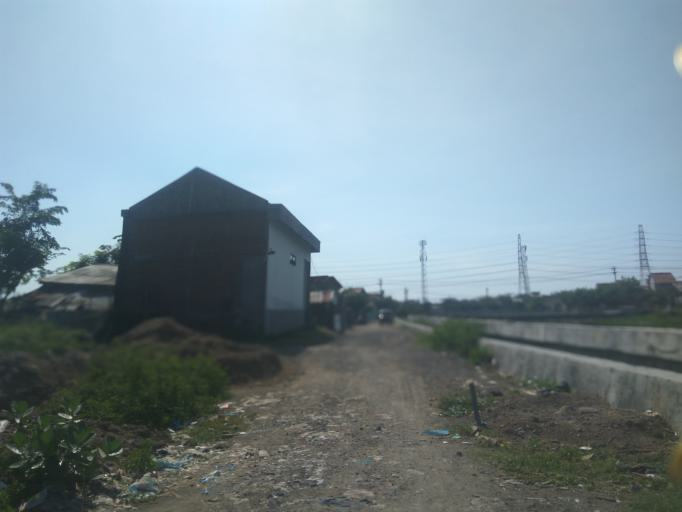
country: ID
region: Central Java
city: Semarang
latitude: -6.9548
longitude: 110.4382
